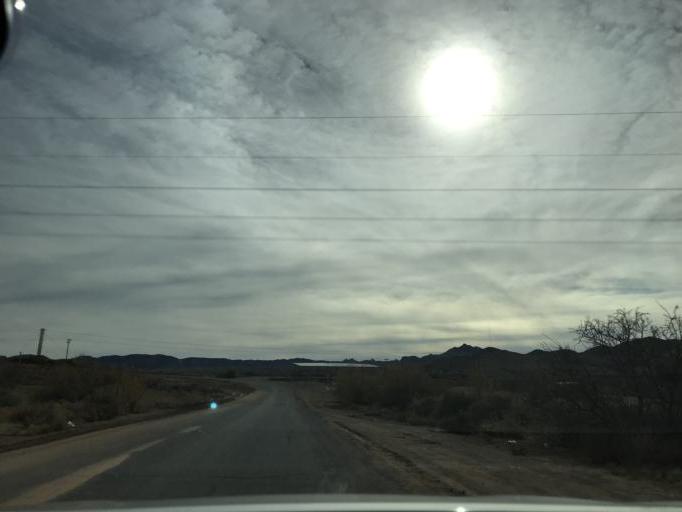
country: US
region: Nevada
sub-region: Clark County
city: Moapa Town
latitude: 36.6612
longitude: -114.5617
